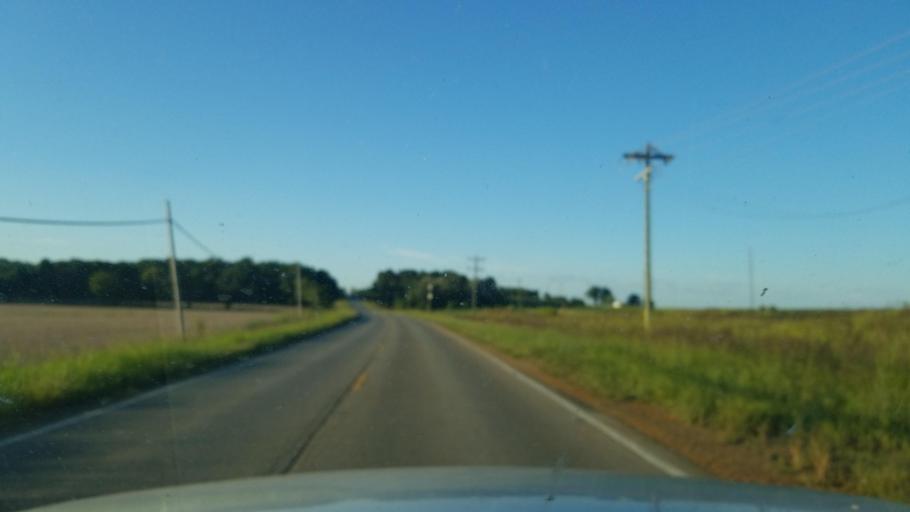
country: US
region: Illinois
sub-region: Saline County
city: Harrisburg
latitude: 37.6657
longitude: -88.5368
